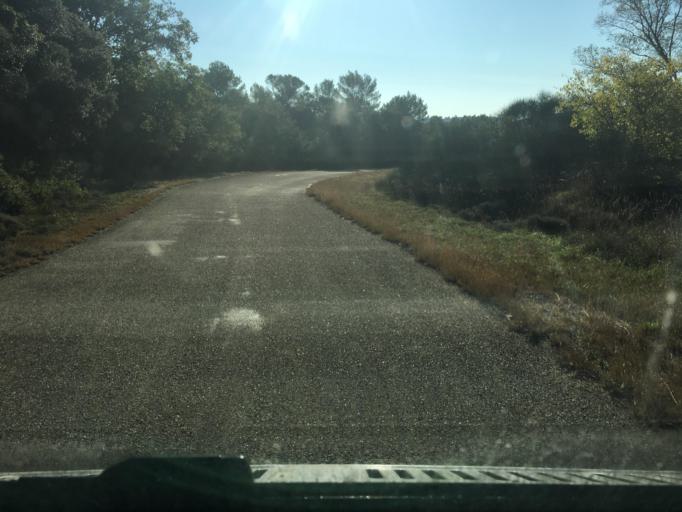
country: FR
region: Languedoc-Roussillon
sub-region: Departement du Gard
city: Goudargues
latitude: 44.1657
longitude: 4.3515
